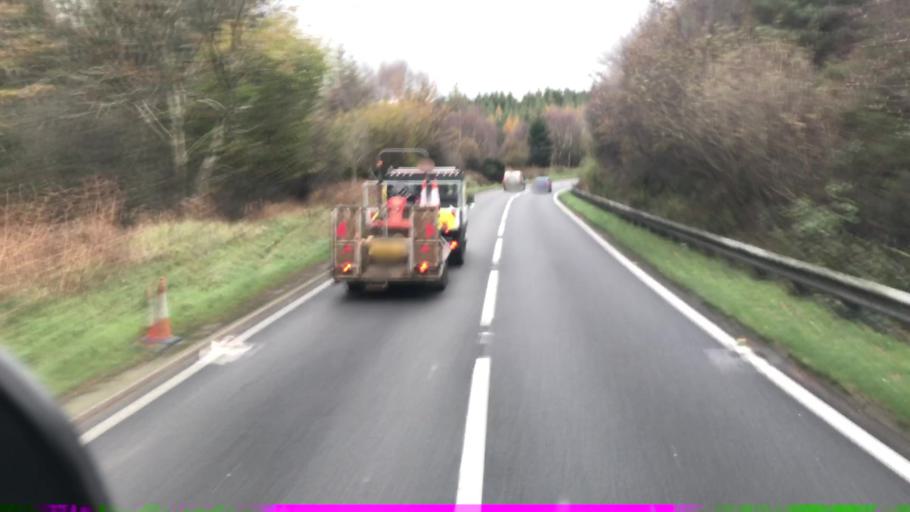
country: GB
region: England
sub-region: Devon
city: Chudleigh
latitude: 50.6350
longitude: -3.5658
